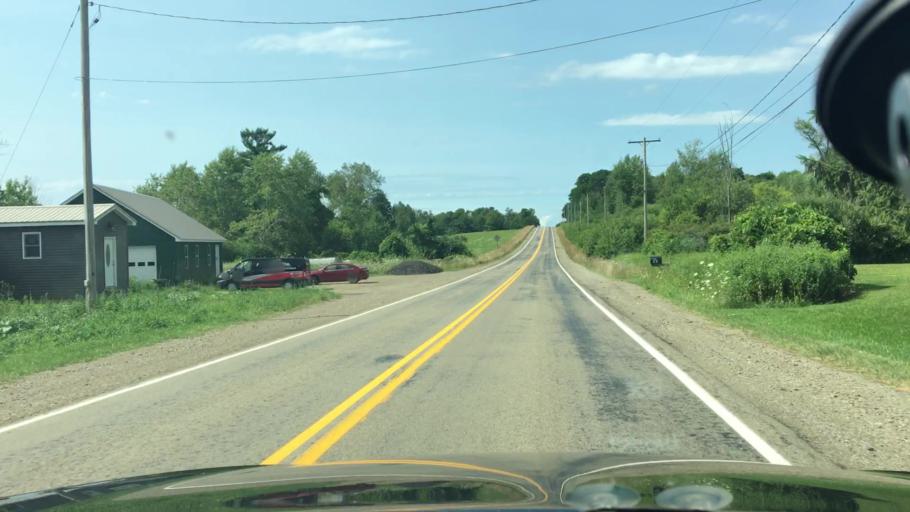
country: US
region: New York
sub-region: Chautauqua County
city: Lakewood
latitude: 42.1863
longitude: -79.3475
